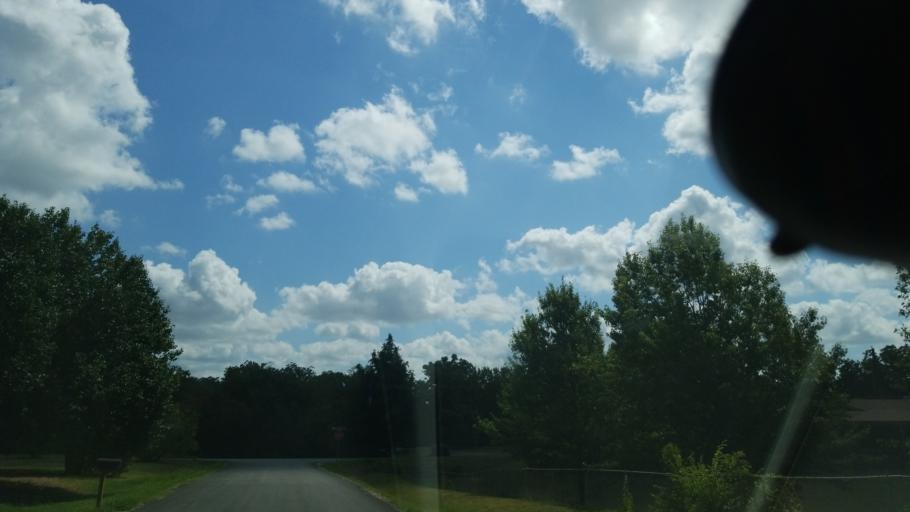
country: US
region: Texas
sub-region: Dallas County
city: Grand Prairie
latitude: 32.7135
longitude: -96.9971
